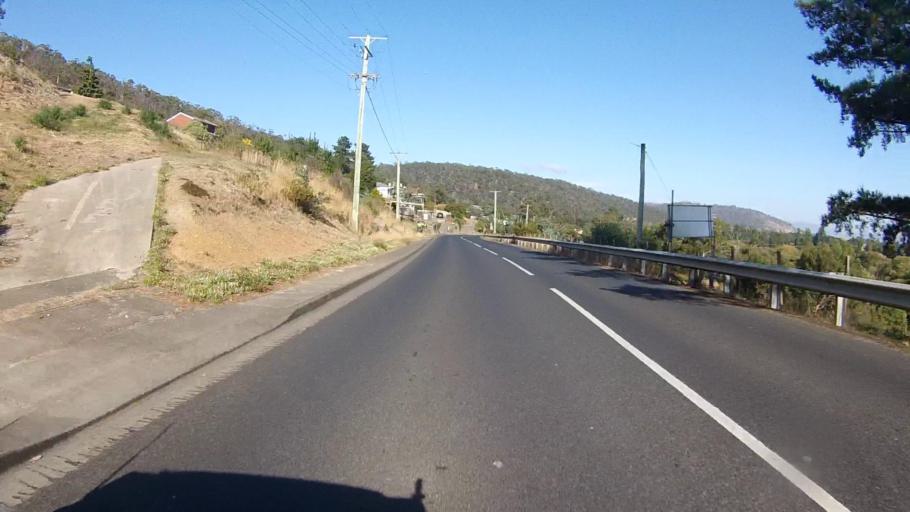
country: AU
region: Tasmania
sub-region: Derwent Valley
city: New Norfolk
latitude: -42.7821
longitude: 147.0523
